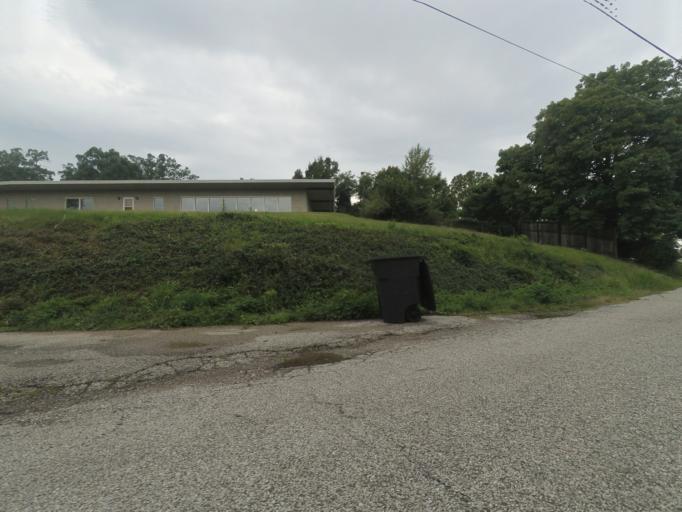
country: US
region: West Virginia
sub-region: Cabell County
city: Huntington
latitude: 38.4025
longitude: -82.4502
